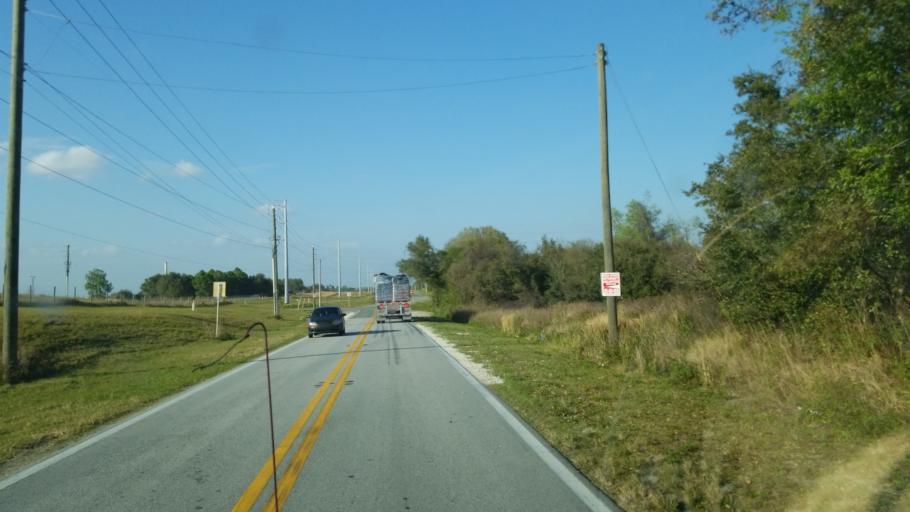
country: US
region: Florida
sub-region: Polk County
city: Mulberry
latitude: 27.7421
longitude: -81.9730
